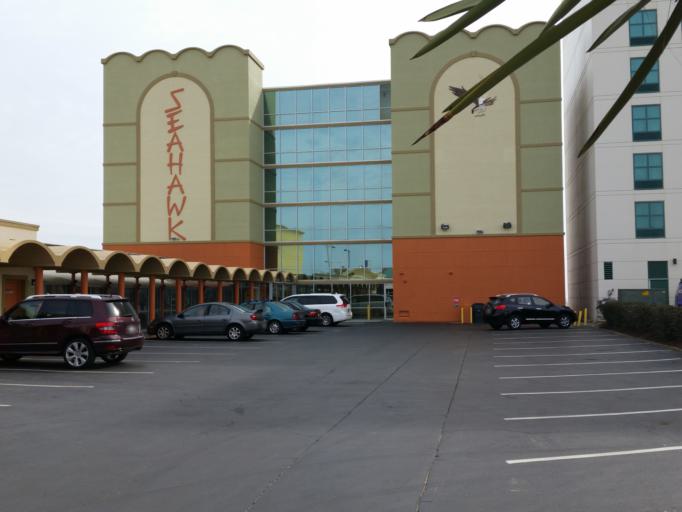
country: US
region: Virginia
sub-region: City of Virginia Beach
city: Virginia Beach
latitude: 36.8542
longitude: -75.9767
